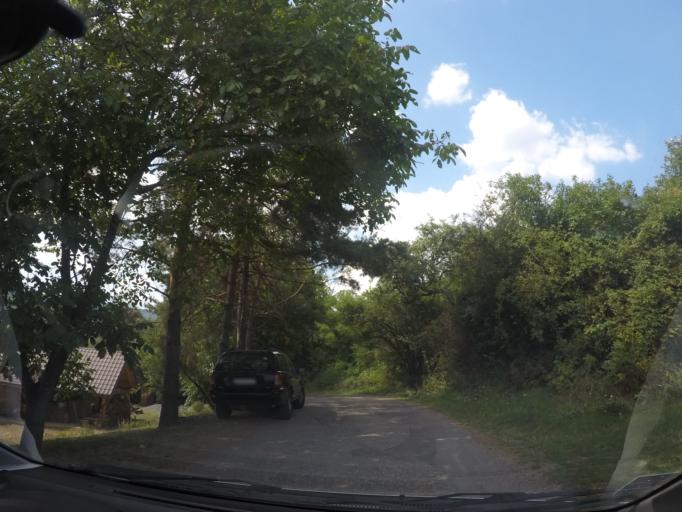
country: SK
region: Banskobystricky
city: Krupina
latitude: 48.3045
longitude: 18.9604
